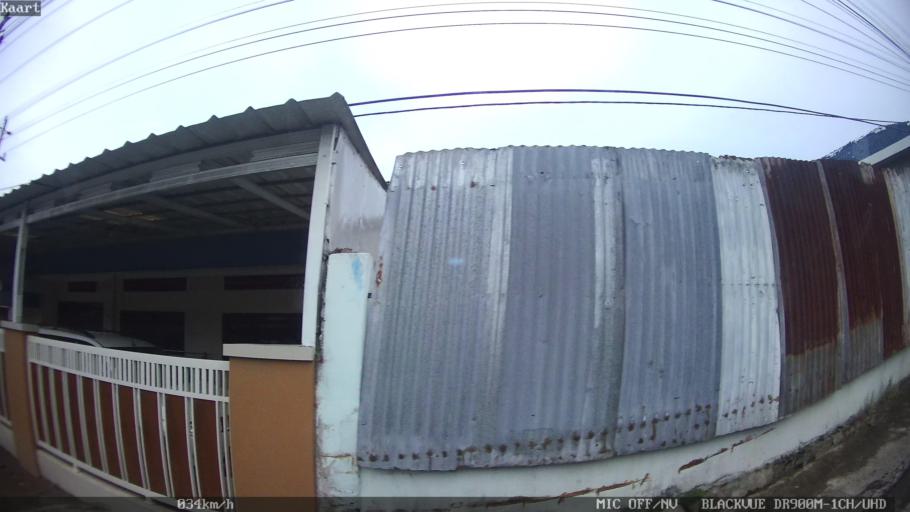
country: ID
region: Lampung
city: Bandarlampung
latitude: -5.4055
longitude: 105.2501
